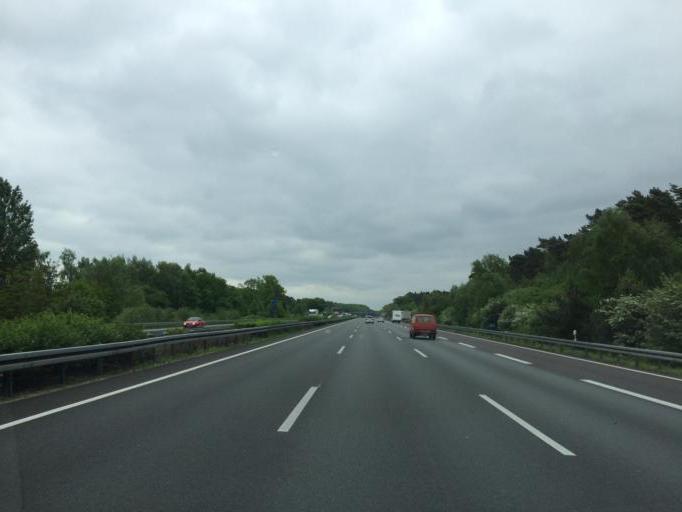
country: DE
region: Lower Saxony
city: Braunschweig
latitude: 52.3131
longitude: 10.5534
